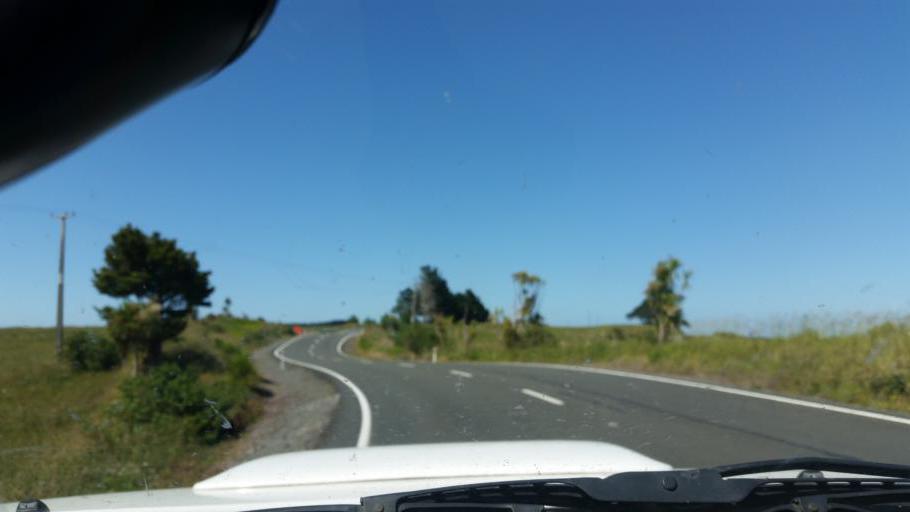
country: NZ
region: Auckland
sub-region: Auckland
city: Wellsford
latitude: -36.2209
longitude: 174.3801
